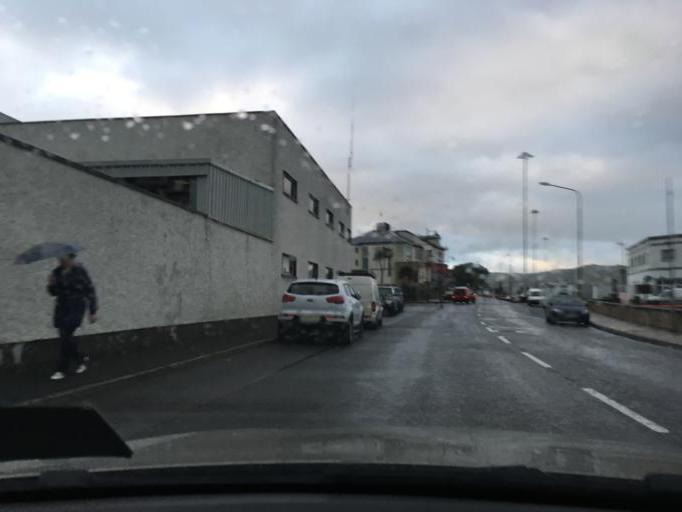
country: IE
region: Ulster
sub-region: County Donegal
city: Killybegs
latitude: 54.6362
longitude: -8.4428
